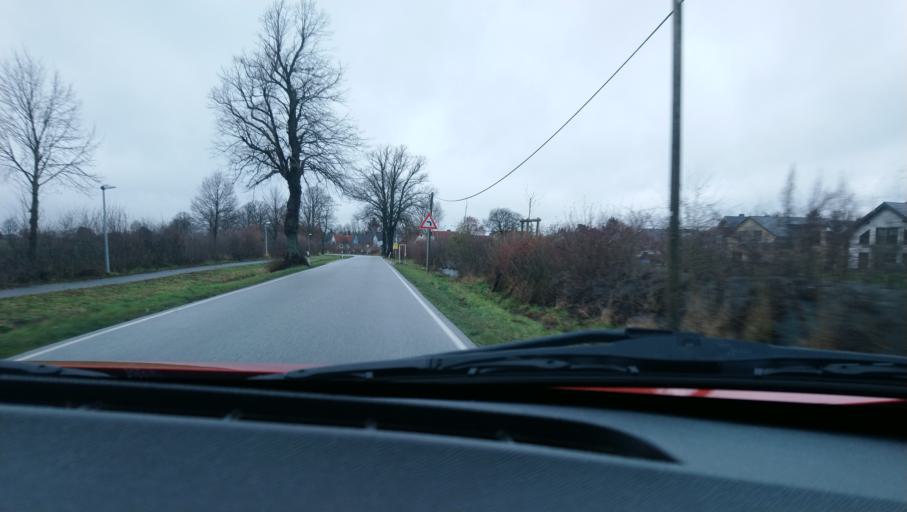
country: DE
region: Mecklenburg-Vorpommern
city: Seehof
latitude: 53.7010
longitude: 11.4329
